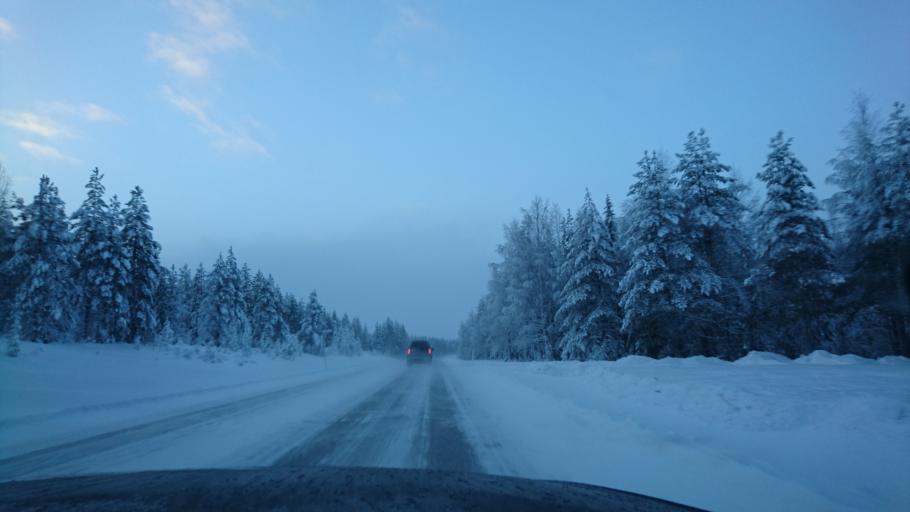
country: FI
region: Northern Ostrobothnia
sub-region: Koillismaa
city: Taivalkoski
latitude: 65.4716
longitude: 27.7353
